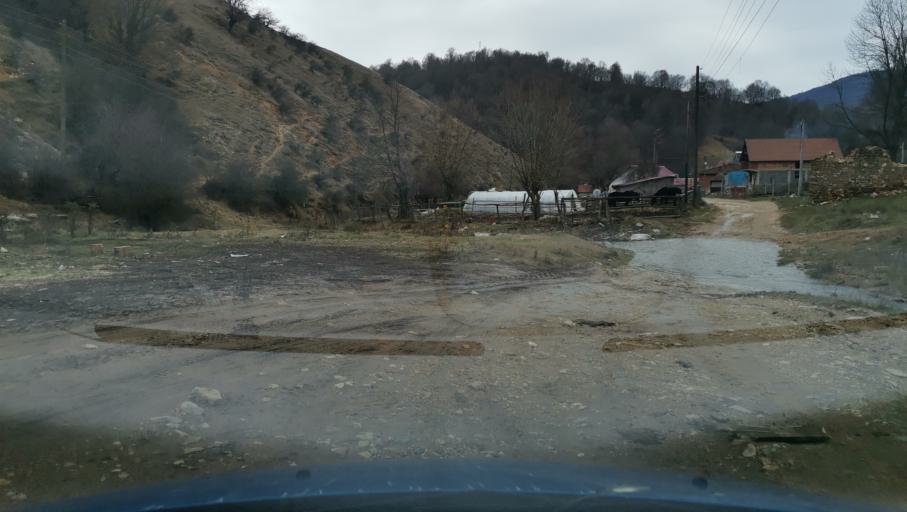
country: MK
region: Berovo
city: Berovo
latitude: 41.5923
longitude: 22.9192
